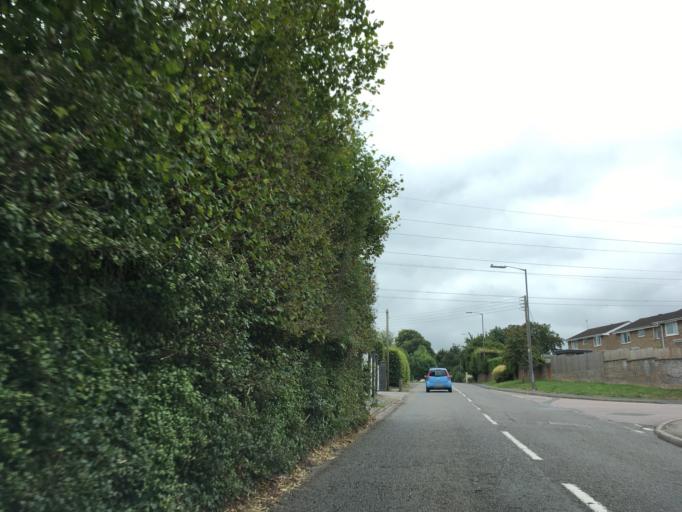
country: GB
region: England
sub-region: South Gloucestershire
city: Bitton
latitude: 51.4354
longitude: -2.4721
